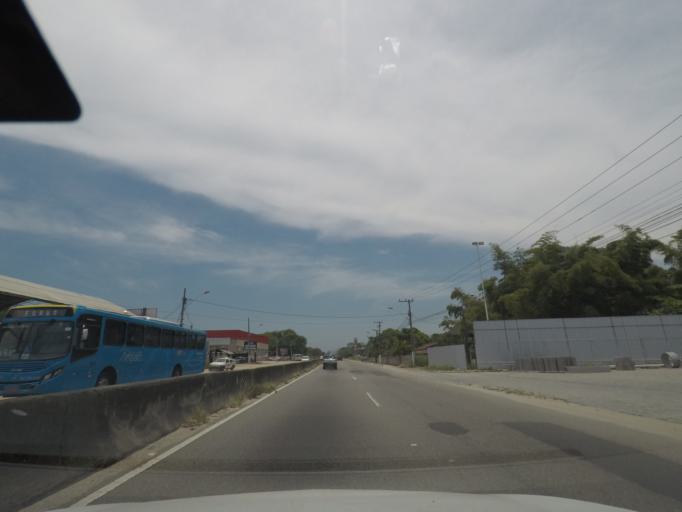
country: BR
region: Rio de Janeiro
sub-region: Marica
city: Marica
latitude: -22.9335
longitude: -42.8939
